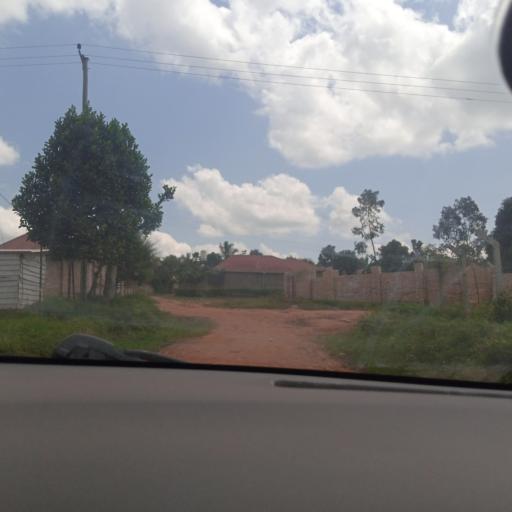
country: UG
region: Central Region
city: Masaka
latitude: -0.3292
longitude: 31.7438
